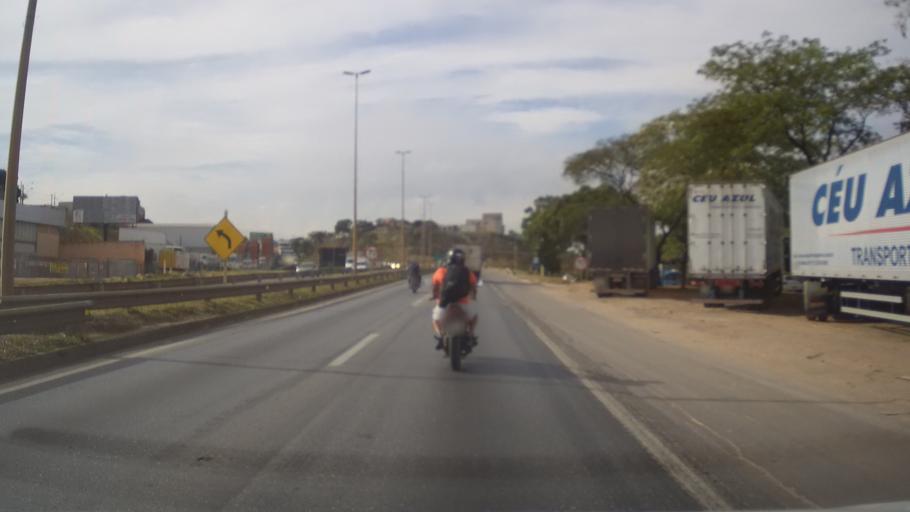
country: BR
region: Minas Gerais
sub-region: Contagem
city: Contagem
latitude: -19.9171
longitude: -44.0396
